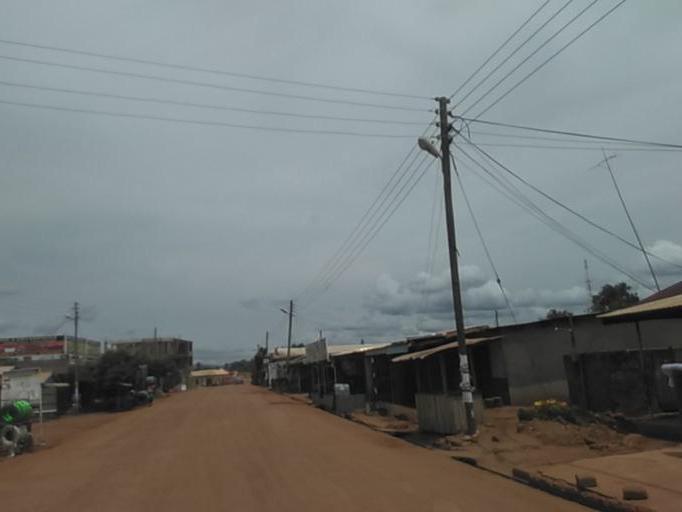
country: GH
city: Akropong
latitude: 6.1373
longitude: 0.0052
